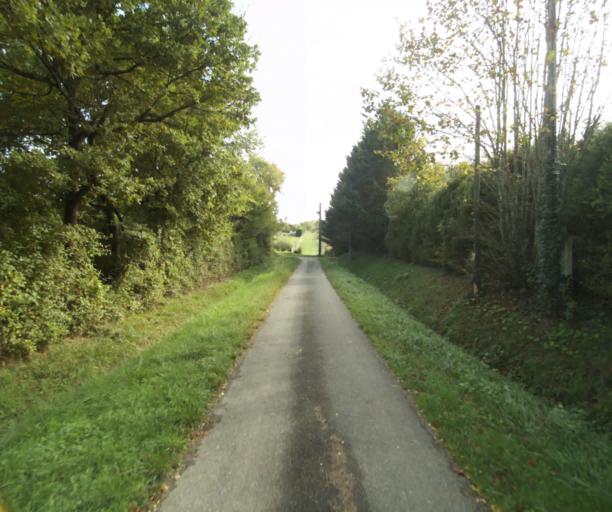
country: FR
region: Midi-Pyrenees
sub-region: Departement du Gers
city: Cazaubon
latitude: 43.8628
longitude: -0.0647
